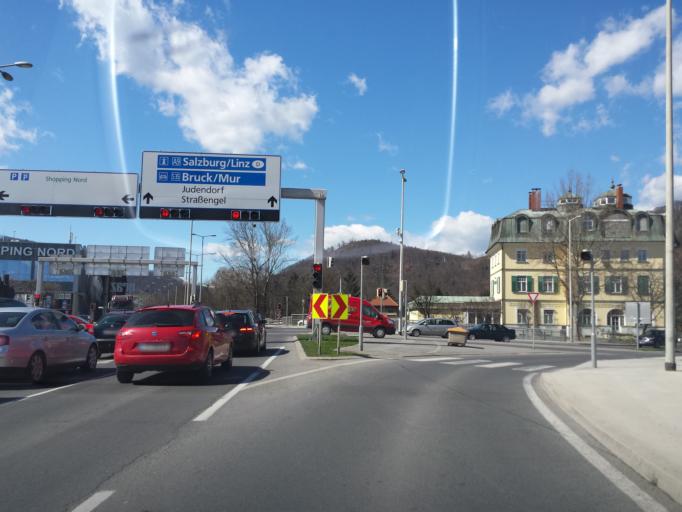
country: AT
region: Styria
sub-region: Graz Stadt
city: Goesting
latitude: 47.1048
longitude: 15.4007
